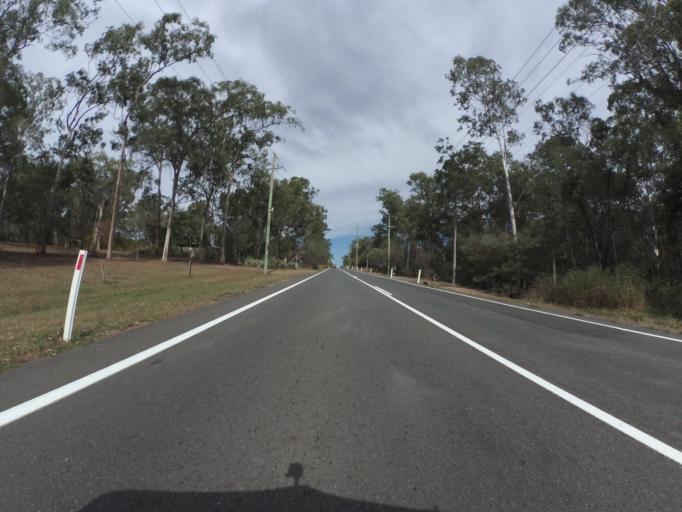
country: AU
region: Queensland
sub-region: Brisbane
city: Riverhills
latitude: -27.5538
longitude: 152.8886
